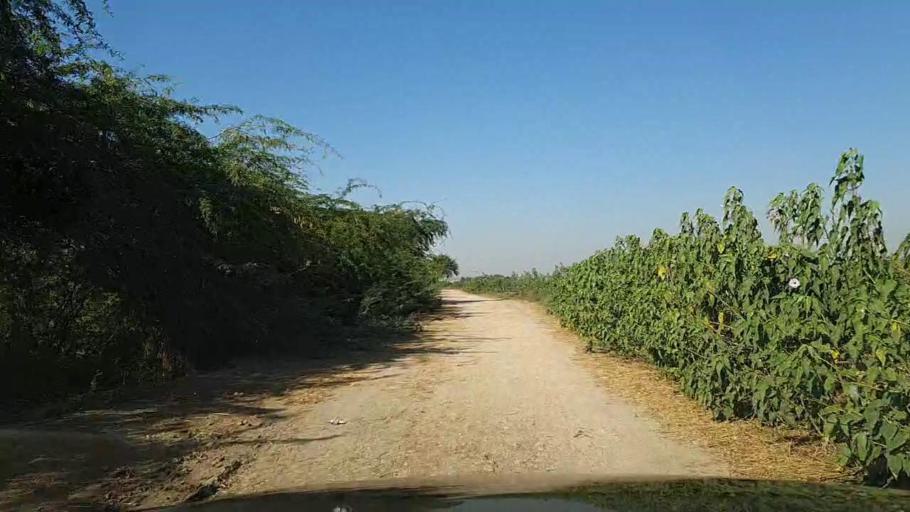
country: PK
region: Sindh
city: Thatta
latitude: 24.7189
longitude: 67.9293
